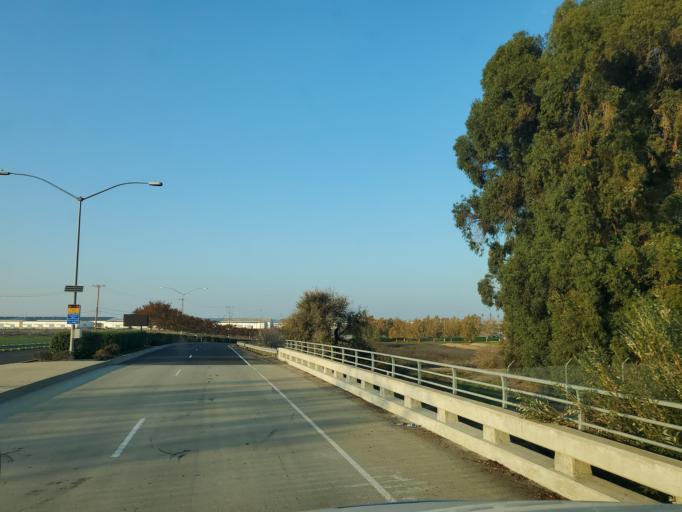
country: US
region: California
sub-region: San Joaquin County
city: Country Club
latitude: 37.9411
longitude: -121.3587
